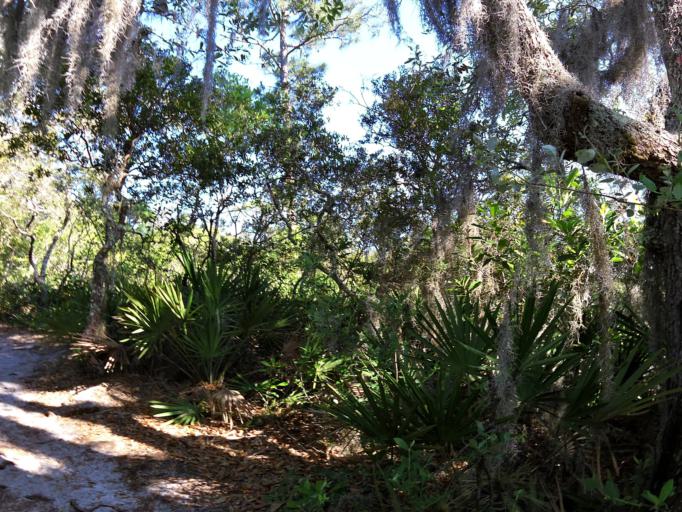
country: US
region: Florida
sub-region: Duval County
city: Atlantic Beach
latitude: 30.3829
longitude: -81.4863
